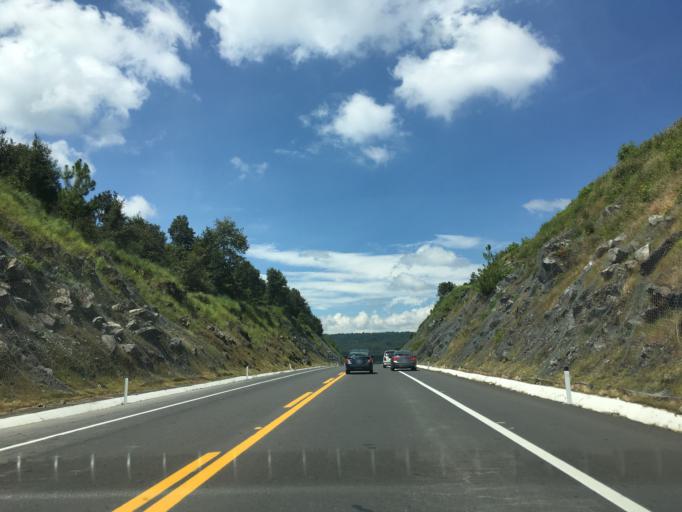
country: MX
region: Michoacan
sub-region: Patzcuaro
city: Colonia Vista Bella (Lomas del Peaje)
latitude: 19.4931
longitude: -101.6105
